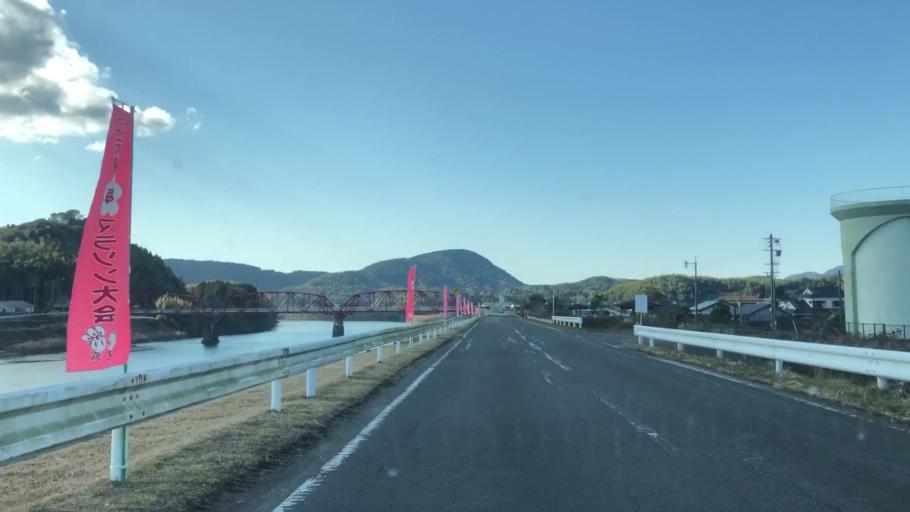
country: JP
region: Kagoshima
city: Satsumasendai
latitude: 31.8614
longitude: 130.3401
